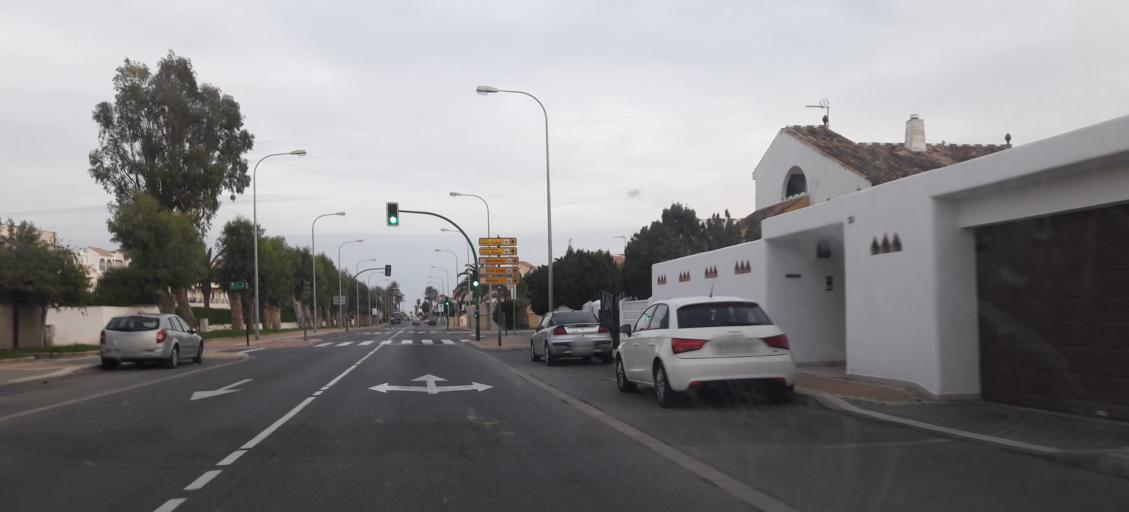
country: ES
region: Andalusia
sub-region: Provincia de Almeria
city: Roquetas de Mar
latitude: 36.7293
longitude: -2.6267
